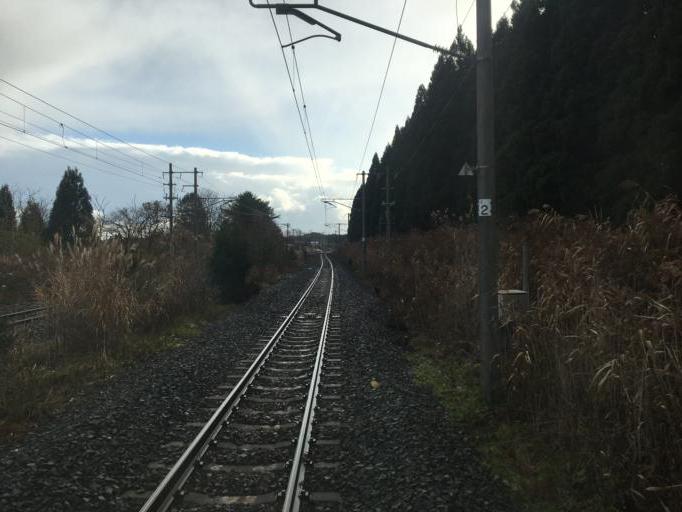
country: JP
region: Aomori
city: Aomori Shi
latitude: 40.9189
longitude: 141.0298
